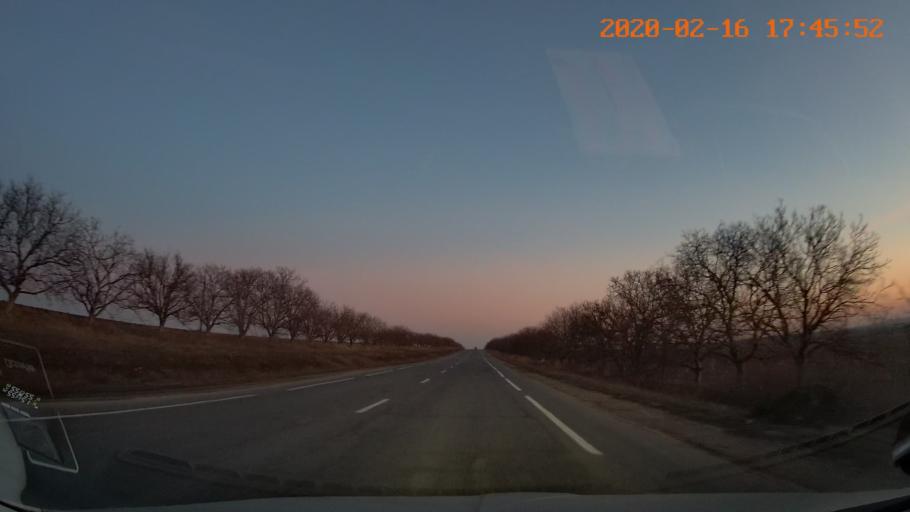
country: MD
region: Riscani
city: Riscani
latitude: 47.9781
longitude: 27.5854
